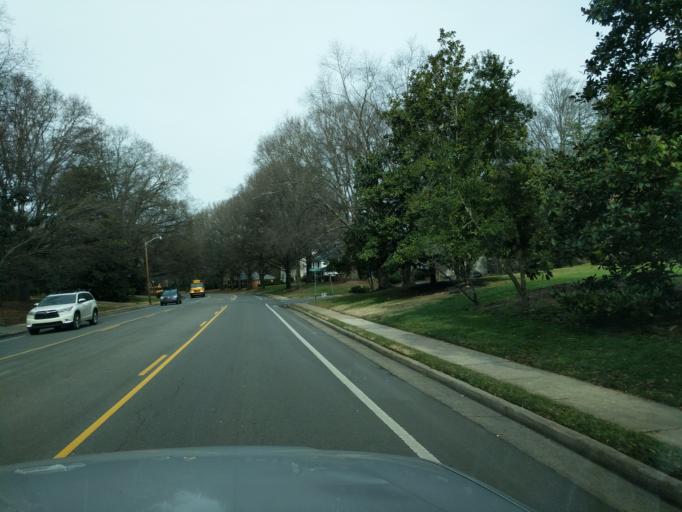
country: US
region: North Carolina
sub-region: Mecklenburg County
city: Charlotte
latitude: 35.1602
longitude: -80.8277
